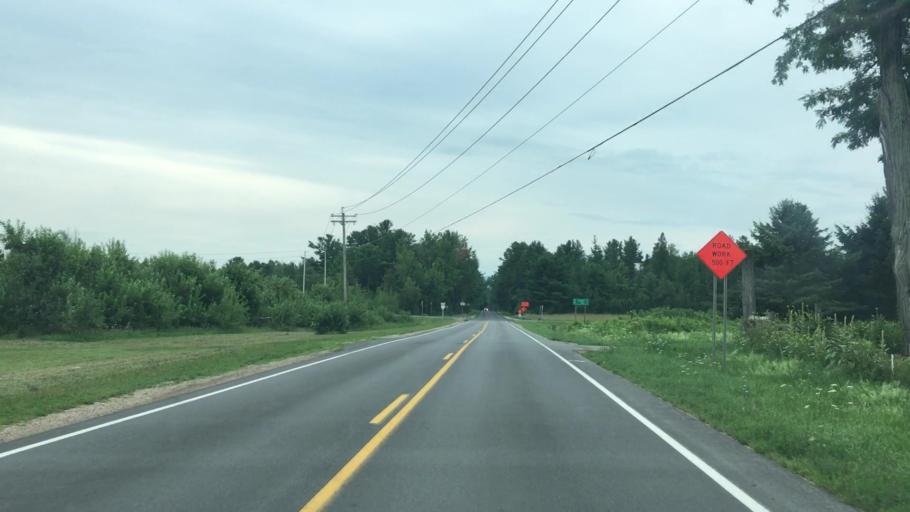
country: US
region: New York
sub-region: Clinton County
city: Peru
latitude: 44.5848
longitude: -73.5710
